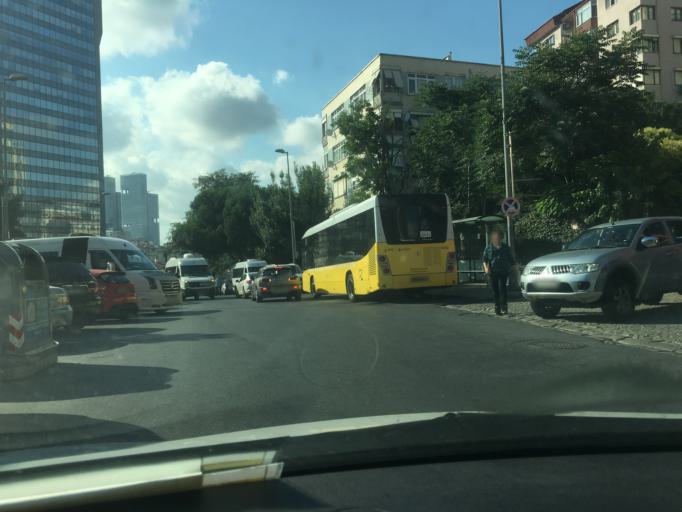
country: TR
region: Istanbul
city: Sisli
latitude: 41.0580
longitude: 29.0091
